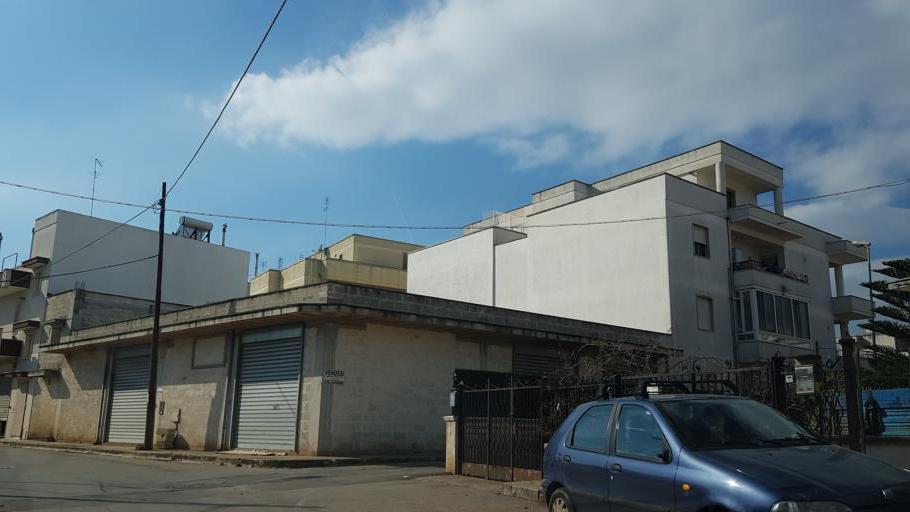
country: IT
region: Apulia
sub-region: Provincia di Brindisi
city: Carovigno
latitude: 40.7117
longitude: 17.6647
